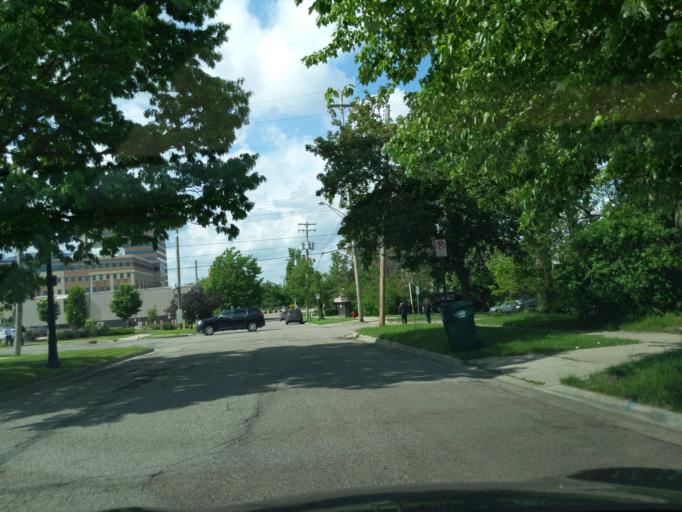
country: US
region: Michigan
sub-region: Ingham County
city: Lansing
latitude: 42.7283
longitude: -84.5492
